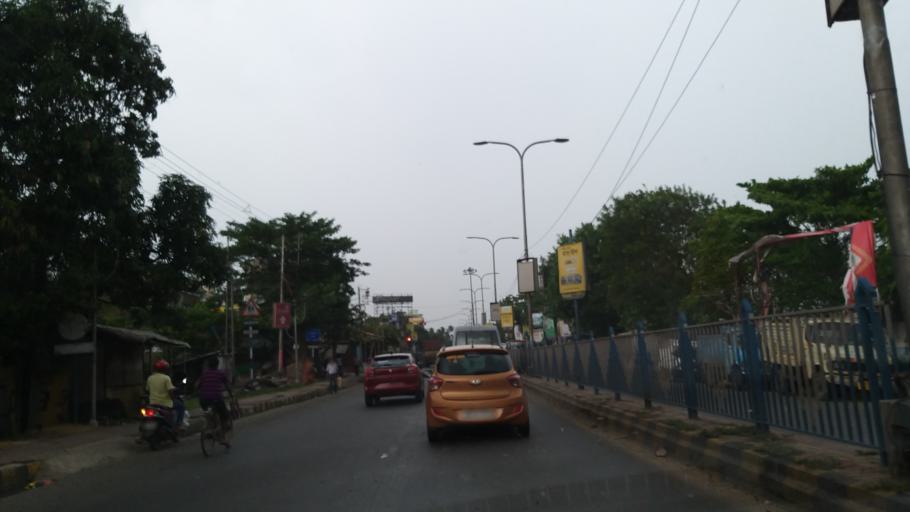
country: IN
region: West Bengal
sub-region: North 24 Parganas
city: Dam Dam
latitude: 22.6582
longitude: 88.4410
